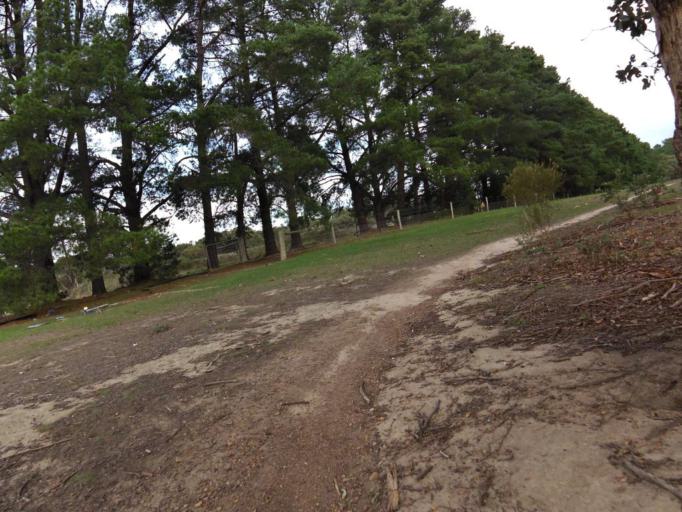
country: AU
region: Victoria
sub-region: Nillumbik
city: Eltham
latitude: -37.7425
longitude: 145.1452
